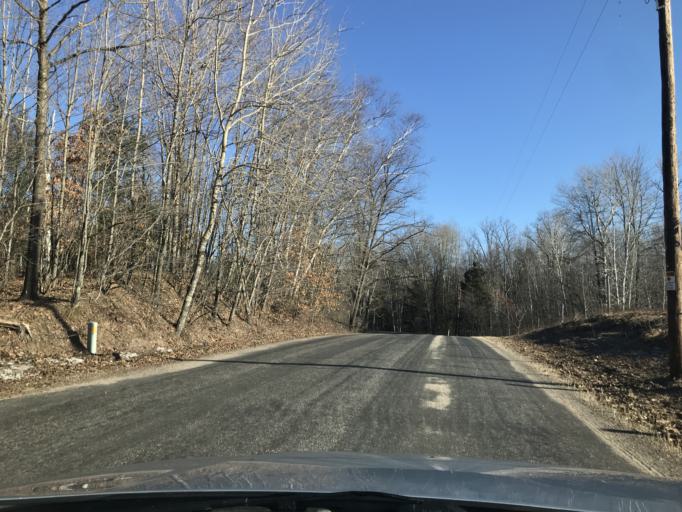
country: US
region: Wisconsin
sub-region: Marinette County
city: Niagara
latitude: 45.3736
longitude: -88.0192
